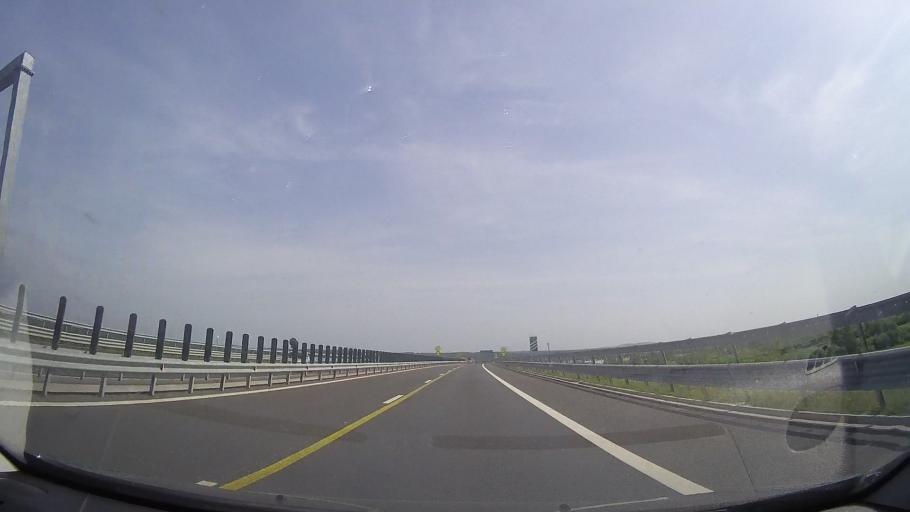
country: RO
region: Timis
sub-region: Comuna Margina
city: Margina
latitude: 45.8549
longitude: 22.2409
